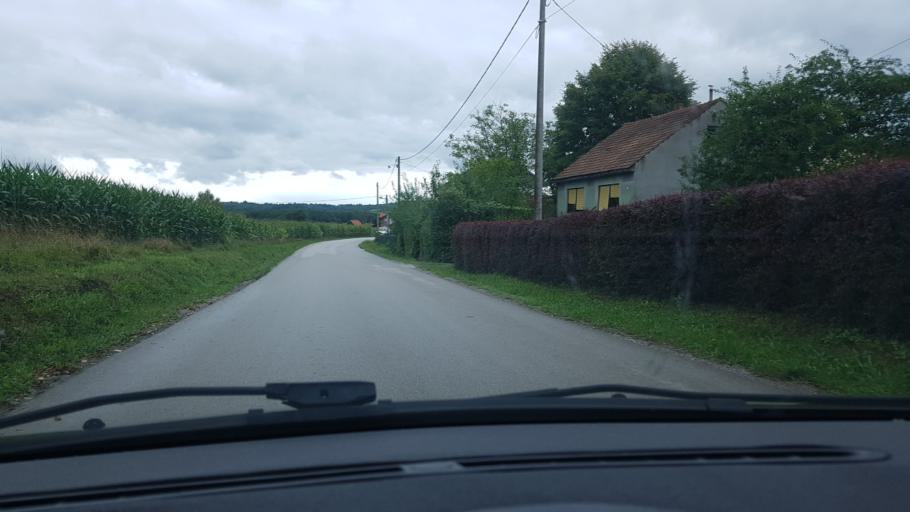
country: HR
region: Karlovacka
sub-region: Grad Karlovac
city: Karlovac
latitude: 45.5527
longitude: 15.5367
